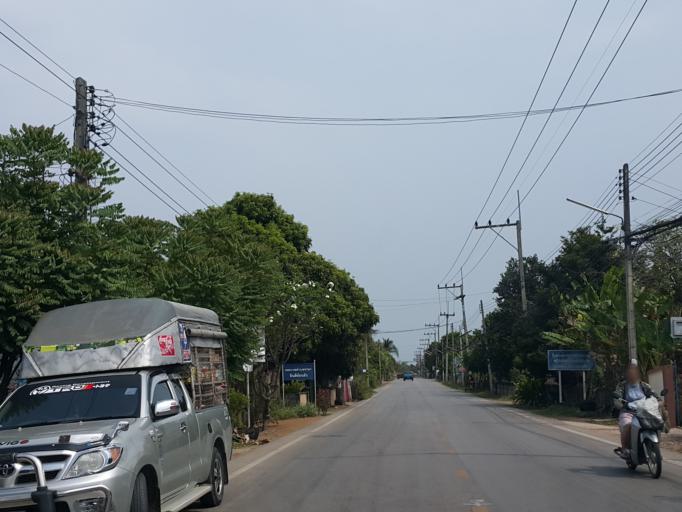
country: TH
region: Lampang
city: Ko Kha
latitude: 18.1573
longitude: 99.3785
